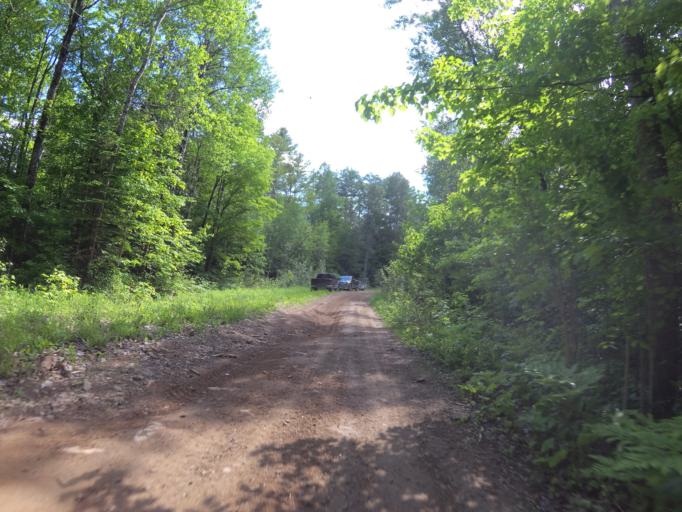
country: CA
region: Ontario
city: Renfrew
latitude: 45.1159
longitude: -76.8748
